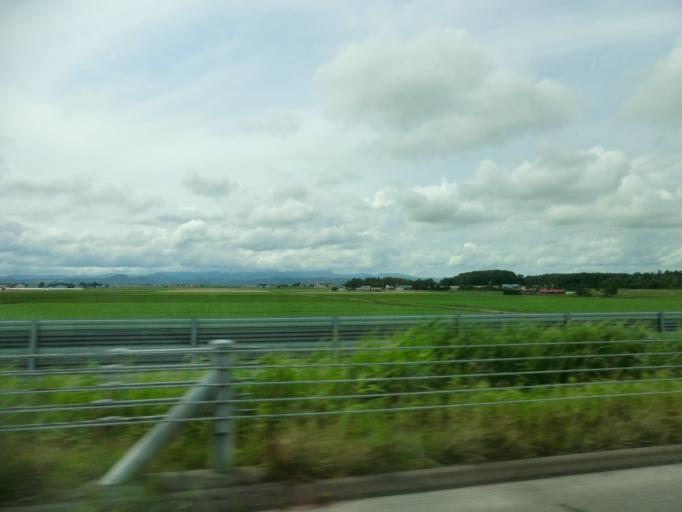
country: JP
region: Hokkaido
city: Takikawa
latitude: 43.5823
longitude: 141.9594
